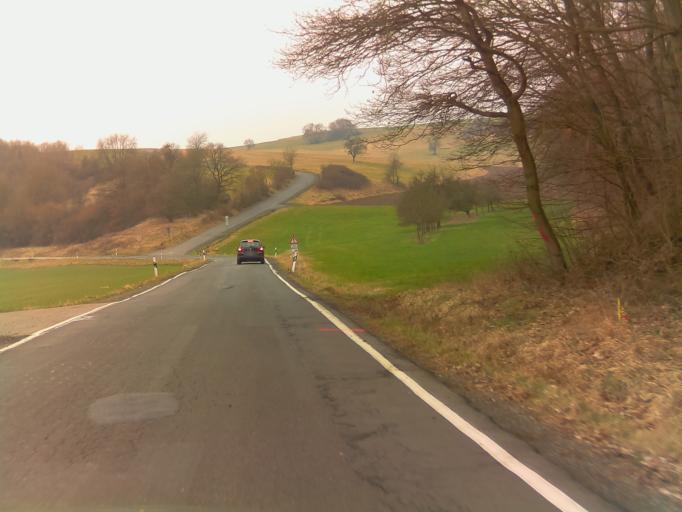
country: DE
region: Rheinland-Pfalz
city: Abtweiler
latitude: 49.7348
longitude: 7.6481
